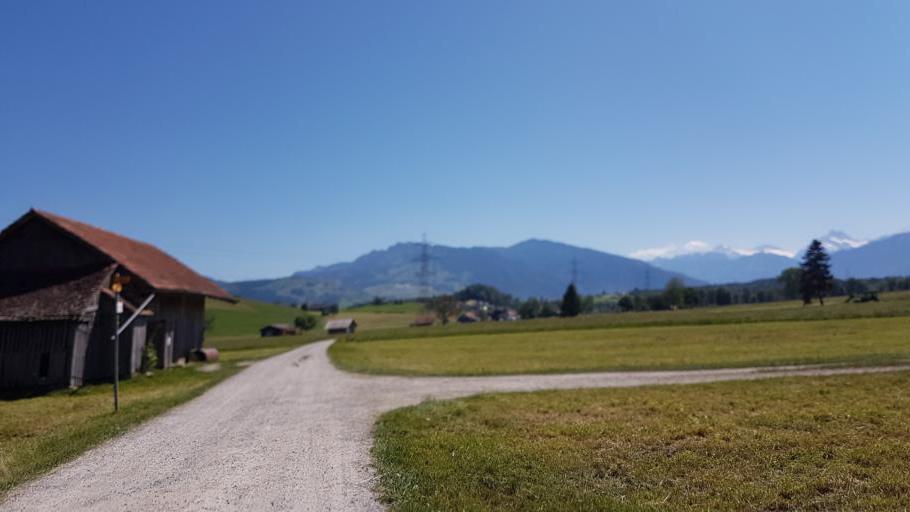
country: CH
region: Bern
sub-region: Frutigen-Niedersimmental District
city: Wimmis
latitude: 46.7040
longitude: 7.6086
